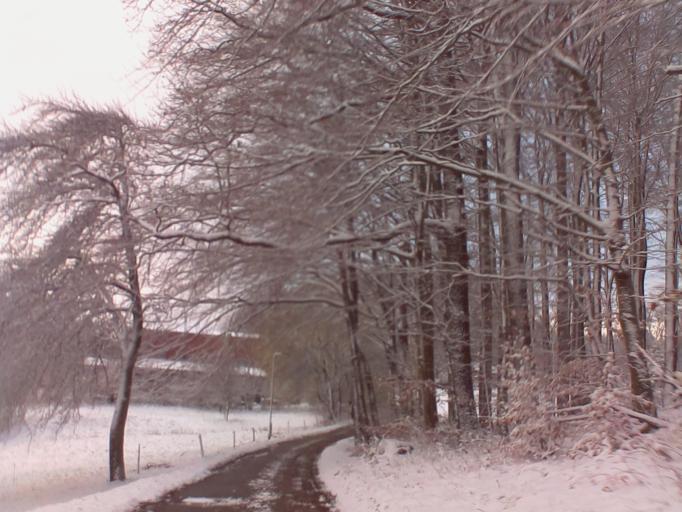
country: DE
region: Hesse
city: Unter-Abtsteinach
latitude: 49.5416
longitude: 8.7914
